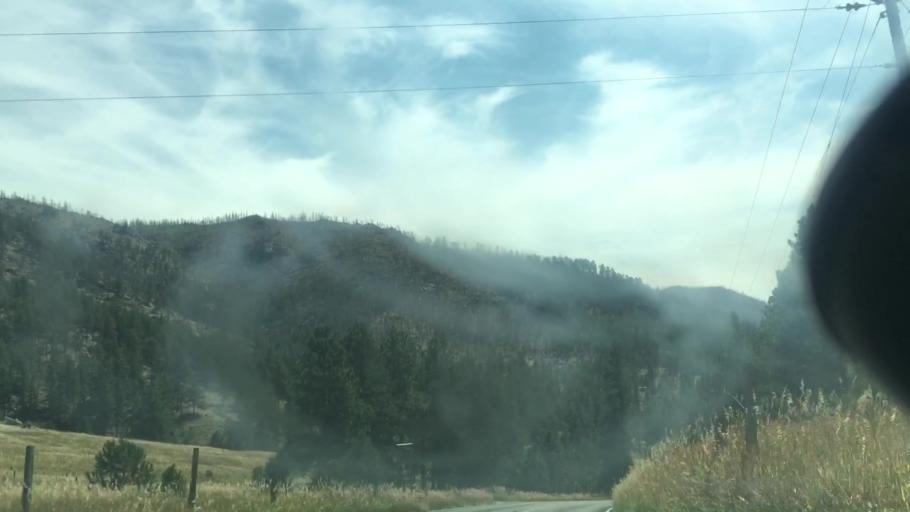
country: US
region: Colorado
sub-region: Larimer County
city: Laporte
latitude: 40.6034
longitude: -105.3431
